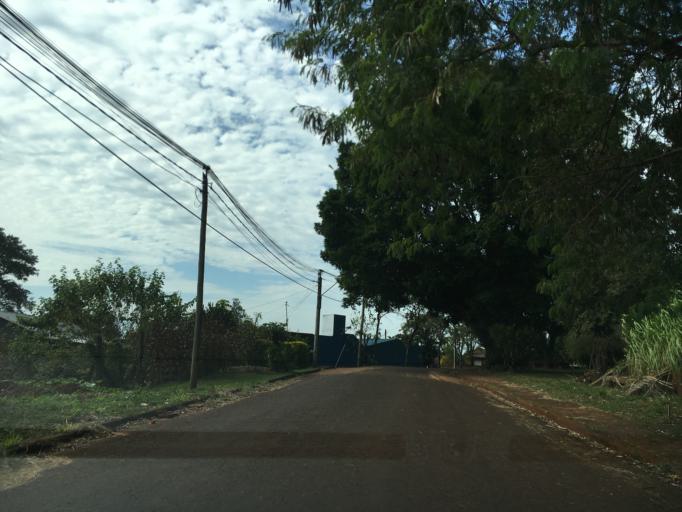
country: AR
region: Misiones
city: Puerto Rico
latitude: -26.7993
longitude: -55.0276
